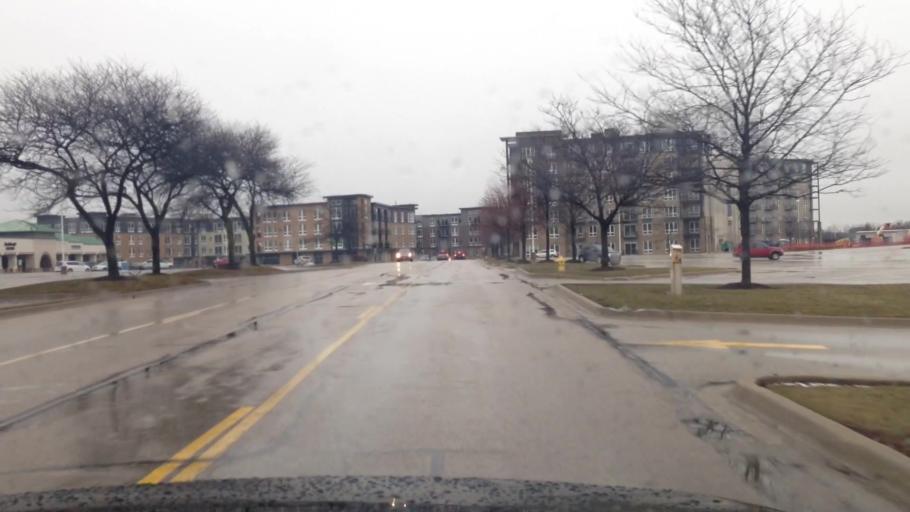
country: US
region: Illinois
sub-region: DuPage County
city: Downers Grove
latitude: 41.8419
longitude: -88.0083
